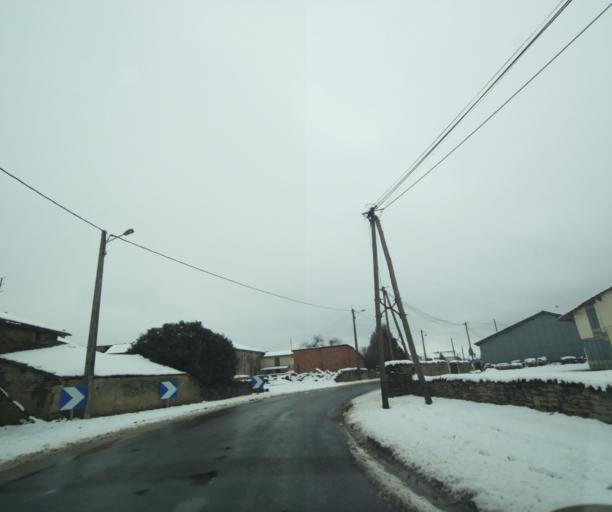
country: FR
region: Champagne-Ardenne
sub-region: Departement de la Haute-Marne
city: Montier-en-Der
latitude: 48.4419
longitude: 4.8034
